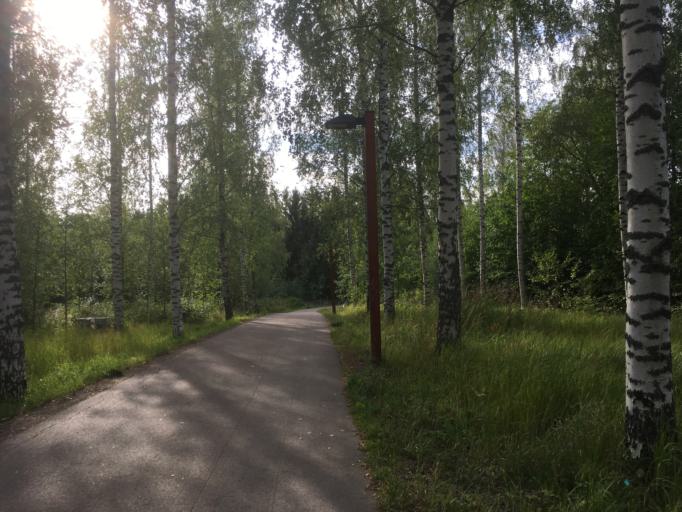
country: FI
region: Central Finland
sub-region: Jyvaeskylae
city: Jyvaeskylae
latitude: 62.2285
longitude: 25.7882
